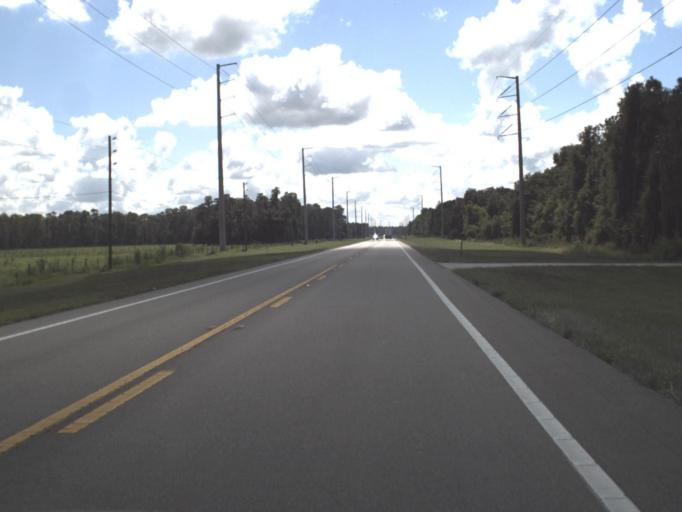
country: US
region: Florida
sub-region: Pasco County
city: Zephyrhills North
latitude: 28.2567
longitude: -82.0712
